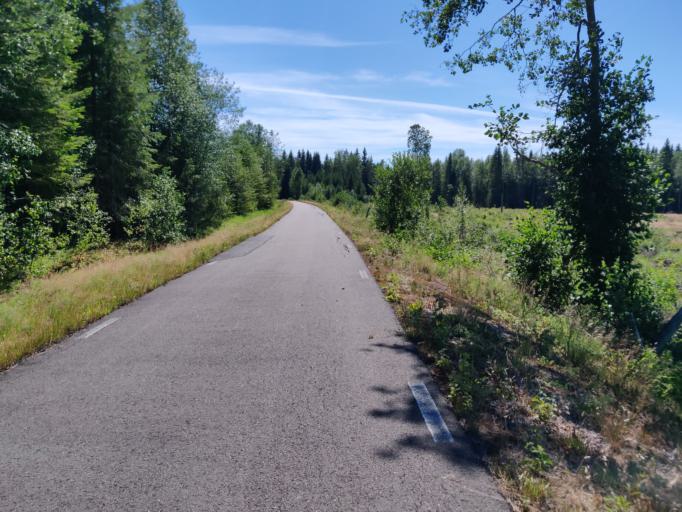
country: SE
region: Vaermland
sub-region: Hagfors Kommun
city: Hagfors
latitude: 59.9758
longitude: 13.5733
